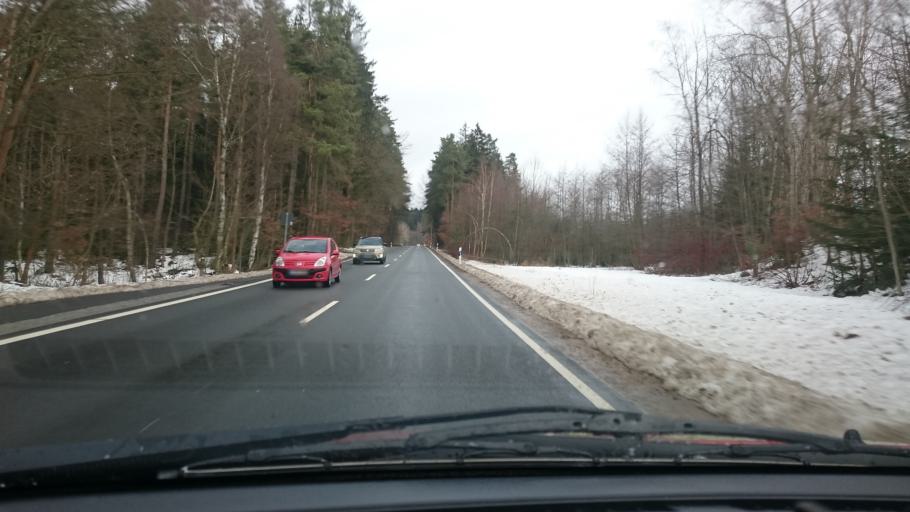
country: DE
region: Saxony
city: Waldkirchen
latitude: 50.5874
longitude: 12.3983
